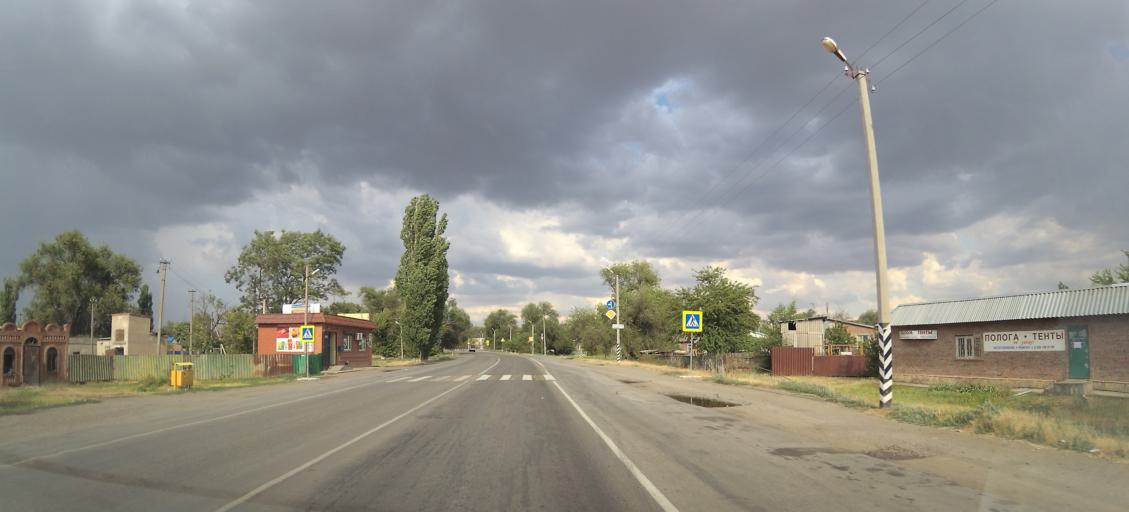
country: RU
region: Rostov
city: Zimovniki
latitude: 47.1461
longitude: 42.4547
